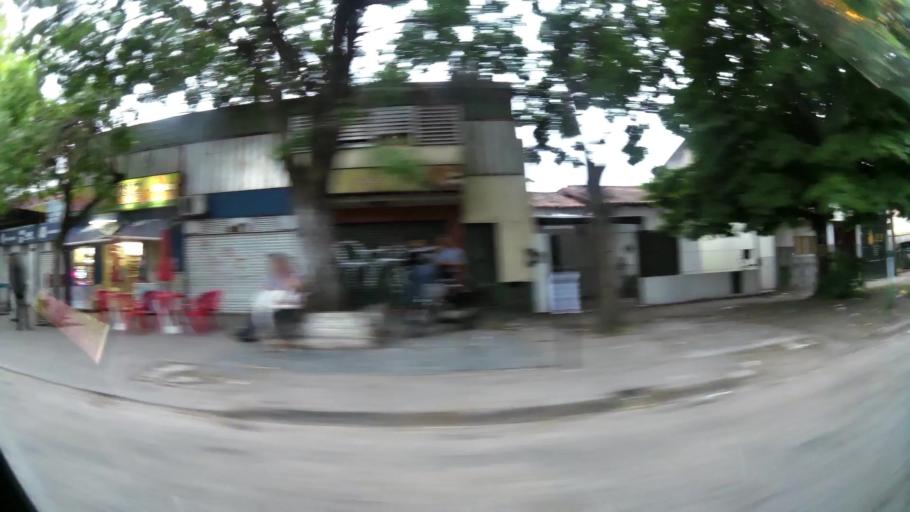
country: AR
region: Buenos Aires
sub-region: Partido de La Plata
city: La Plata
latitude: -34.9056
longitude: -57.9754
